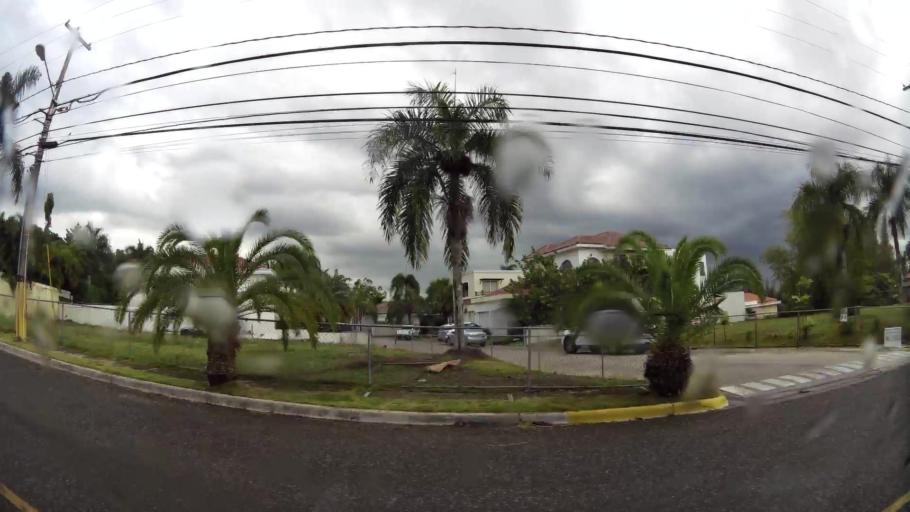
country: DO
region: Nacional
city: La Agustina
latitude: 18.5128
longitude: -69.9357
